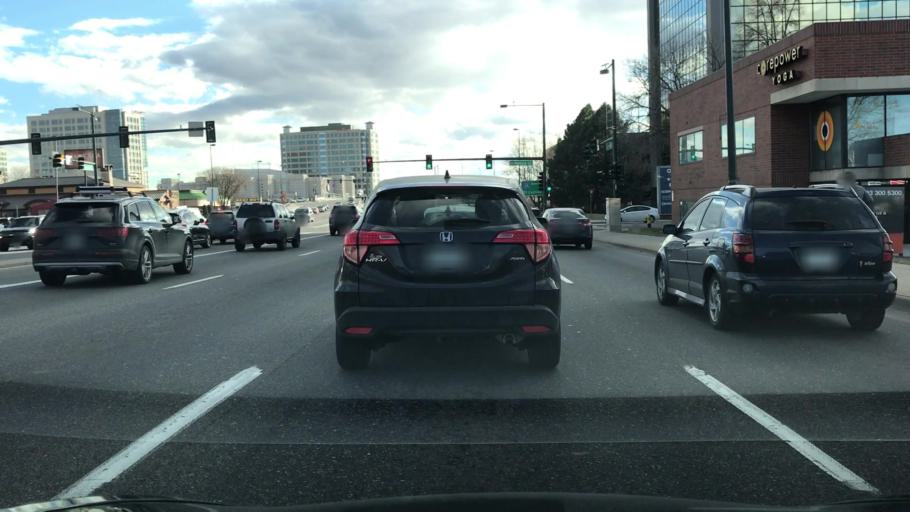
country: US
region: Colorado
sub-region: Arapahoe County
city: Glendale
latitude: 39.6863
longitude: -104.9409
